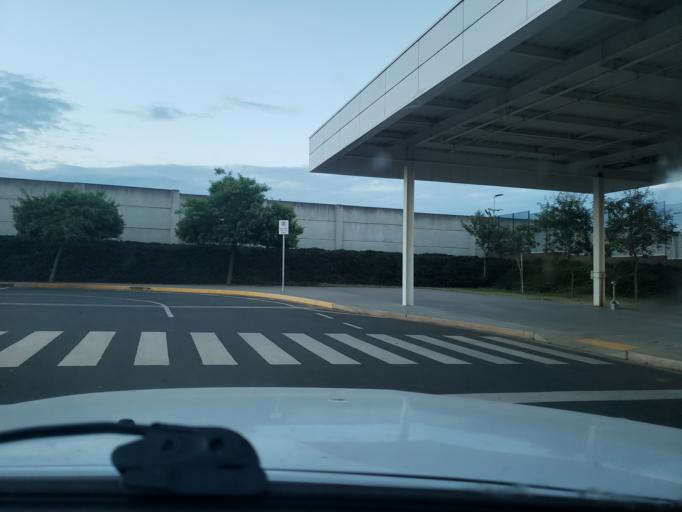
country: BR
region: Sao Paulo
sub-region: Mogi-Mirim
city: Mogi Mirim
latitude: -22.4892
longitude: -46.9737
